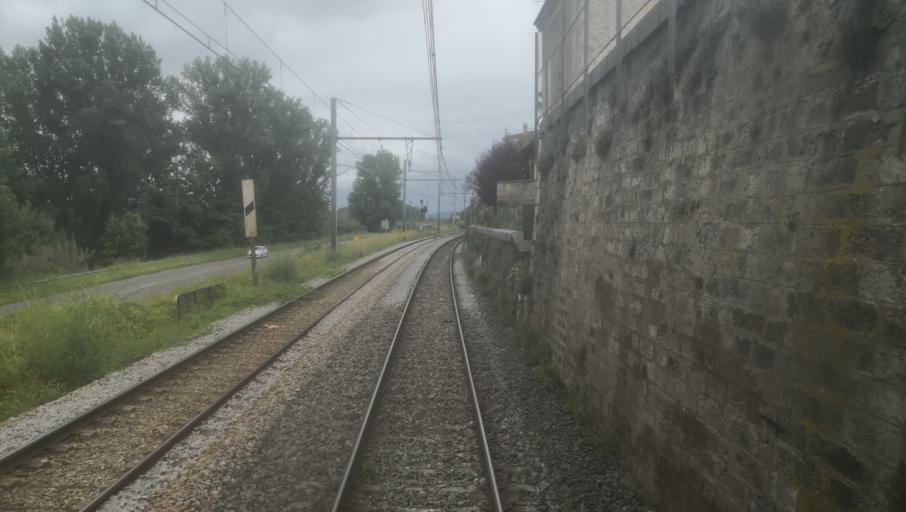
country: FR
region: Aquitaine
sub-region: Departement du Lot-et-Garonne
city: Port-Sainte-Marie
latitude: 44.2502
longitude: 0.3994
